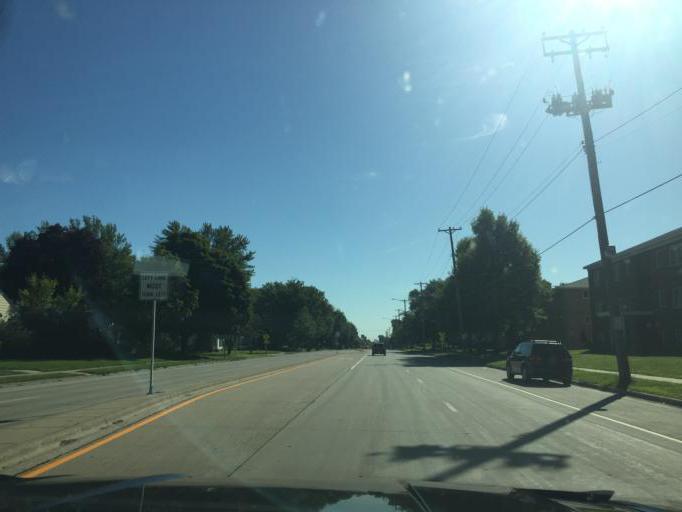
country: US
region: Minnesota
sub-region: Ramsey County
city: Falcon Heights
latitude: 44.9917
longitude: -93.1630
